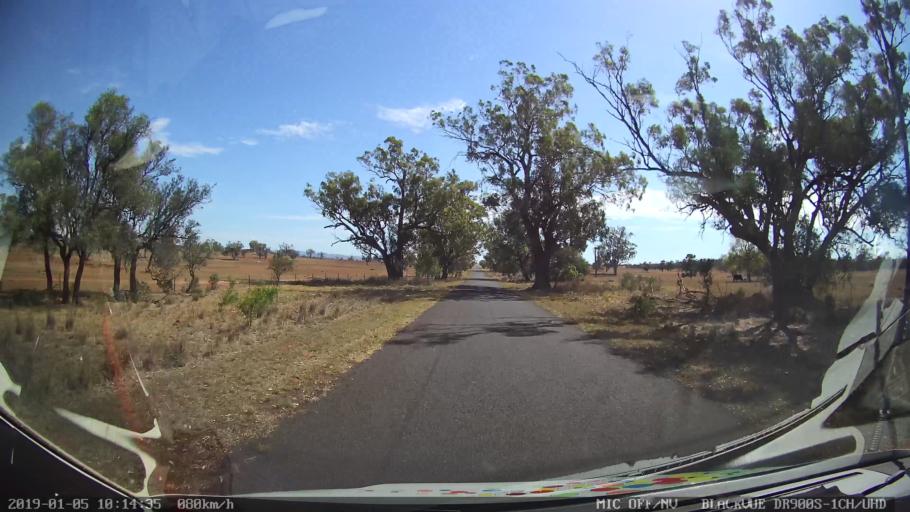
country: AU
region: New South Wales
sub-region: Gilgandra
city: Gilgandra
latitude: -31.5916
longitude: 148.9357
